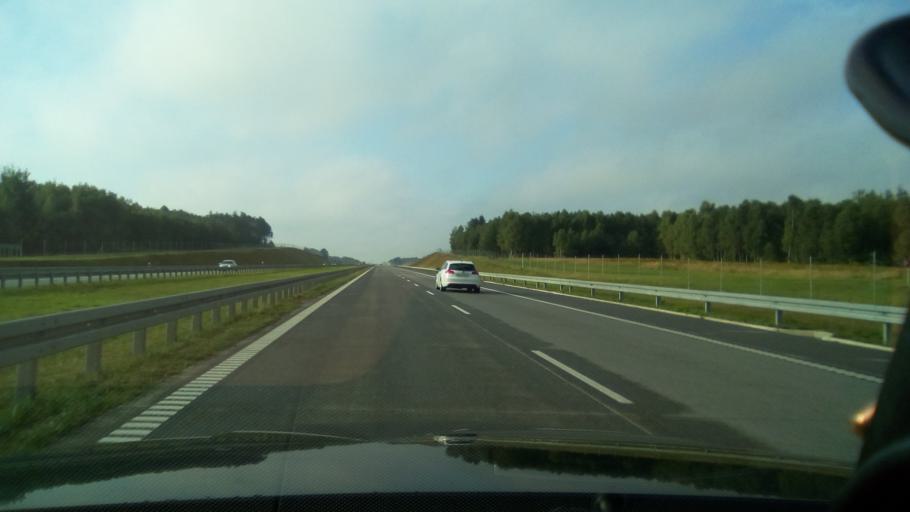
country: PL
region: Silesian Voivodeship
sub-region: Powiat czestochowski
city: Konopiska
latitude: 50.7151
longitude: 19.0569
